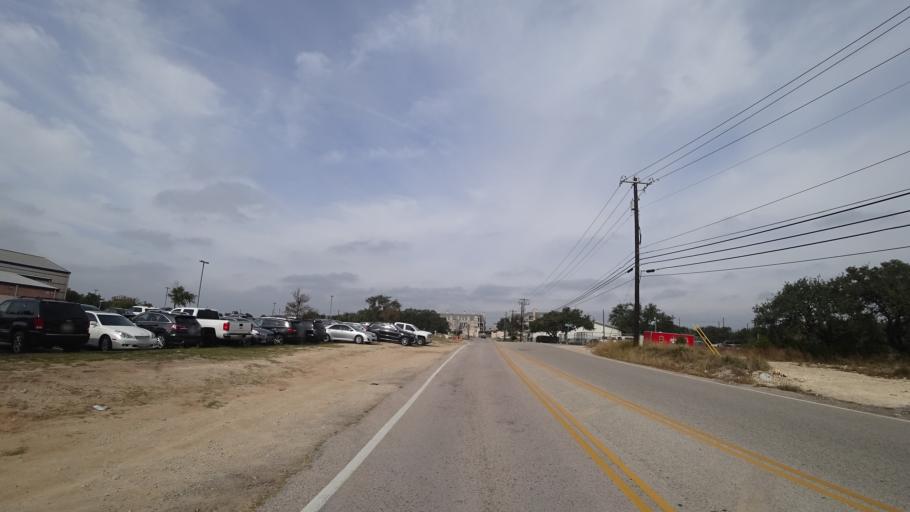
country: US
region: Texas
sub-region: Travis County
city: Hudson Bend
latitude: 30.3917
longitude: -97.9340
